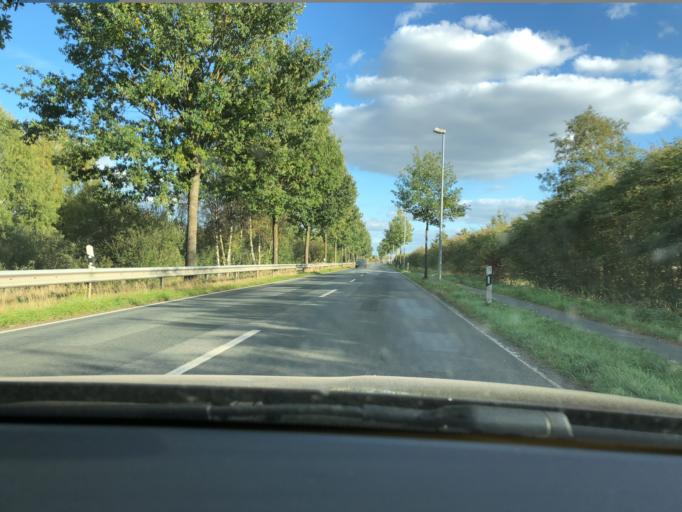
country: DE
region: Lower Saxony
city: Stuhr
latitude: 53.0269
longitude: 8.7561
